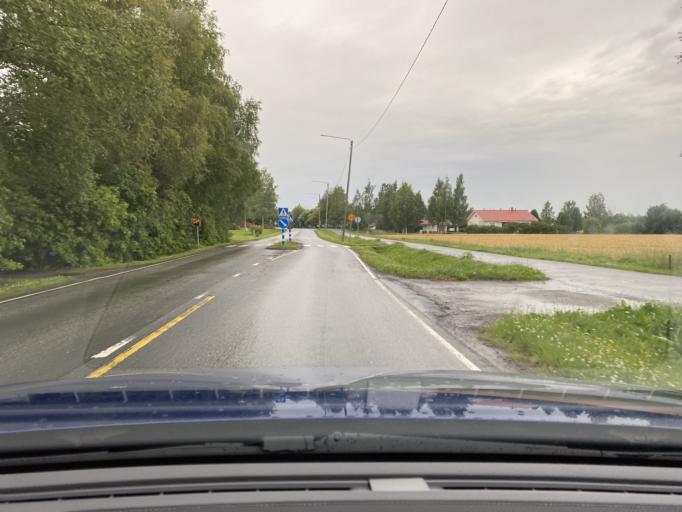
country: FI
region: Ostrobothnia
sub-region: Kyroenmaa
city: Laihia
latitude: 62.9796
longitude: 21.9971
